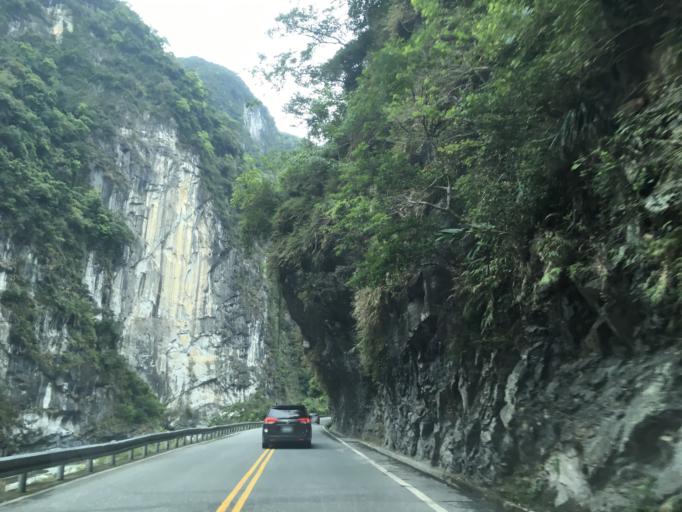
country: TW
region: Taiwan
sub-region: Hualien
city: Hualian
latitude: 24.1651
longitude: 121.6053
